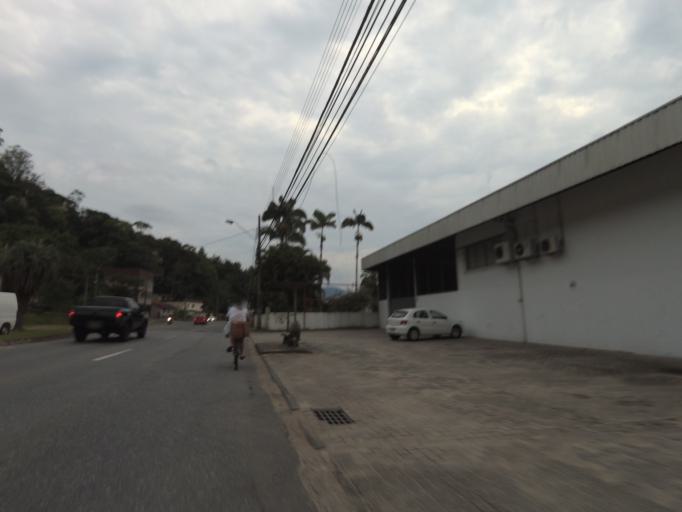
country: BR
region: Santa Catarina
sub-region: Blumenau
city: Blumenau
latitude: -26.9019
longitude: -49.0625
